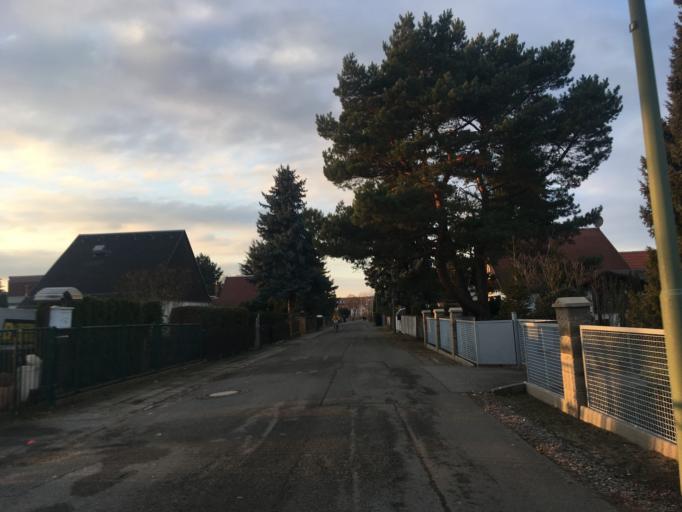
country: DE
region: Berlin
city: Karow
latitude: 52.6195
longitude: 13.4927
